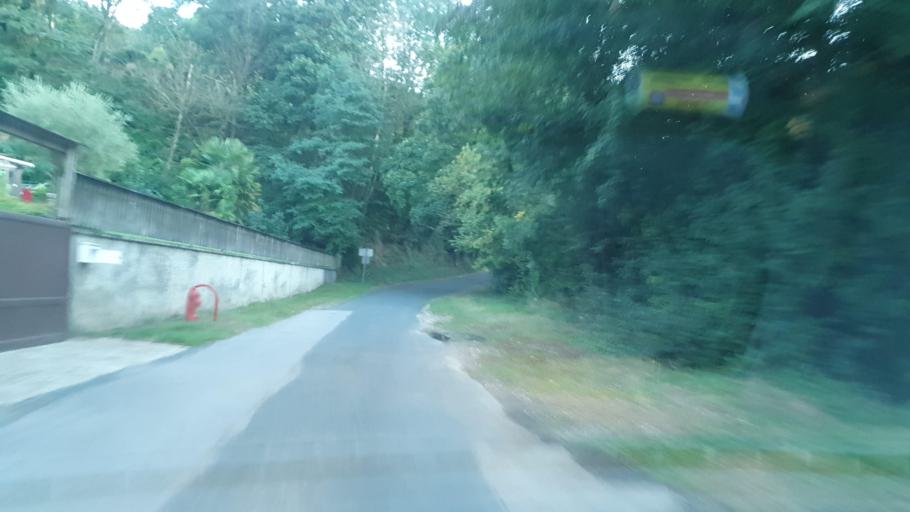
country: FR
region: Rhone-Alpes
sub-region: Departement du Rhone
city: Fleurieu-sur-Saone
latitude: 45.8566
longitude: 4.8446
